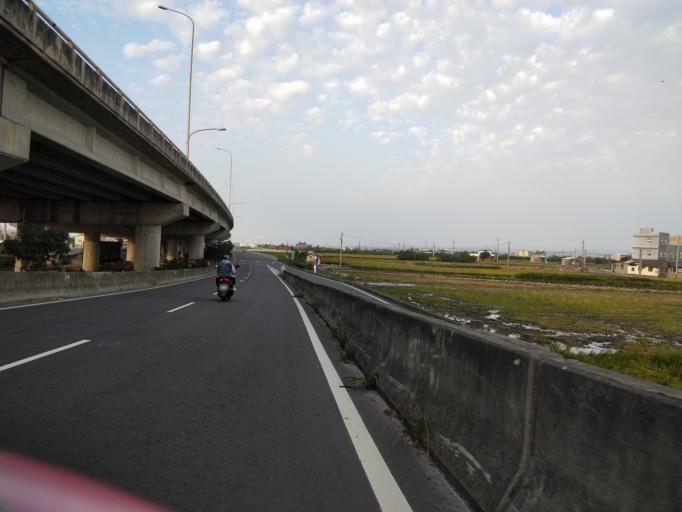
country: TW
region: Taiwan
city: Fengyuan
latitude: 24.4046
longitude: 120.6133
